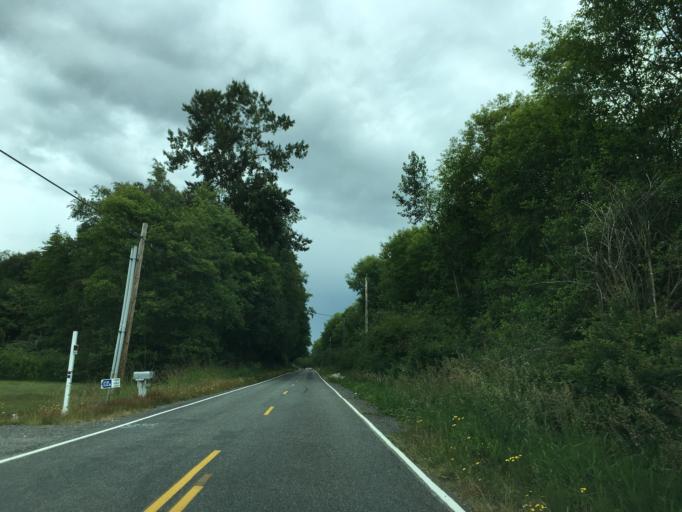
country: US
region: Washington
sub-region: Whatcom County
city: Birch Bay
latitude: 48.9432
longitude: -122.7460
